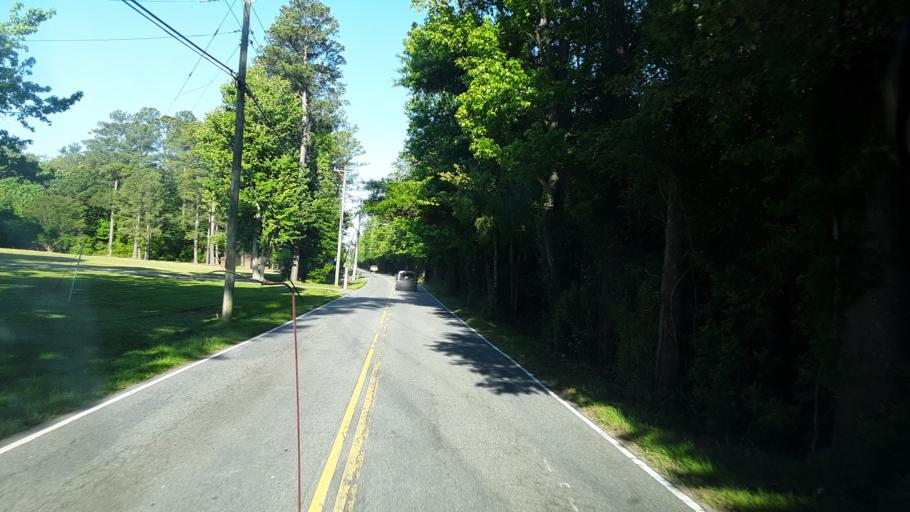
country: US
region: Virginia
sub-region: City of Virginia Beach
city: Virginia Beach
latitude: 36.7233
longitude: -76.0216
